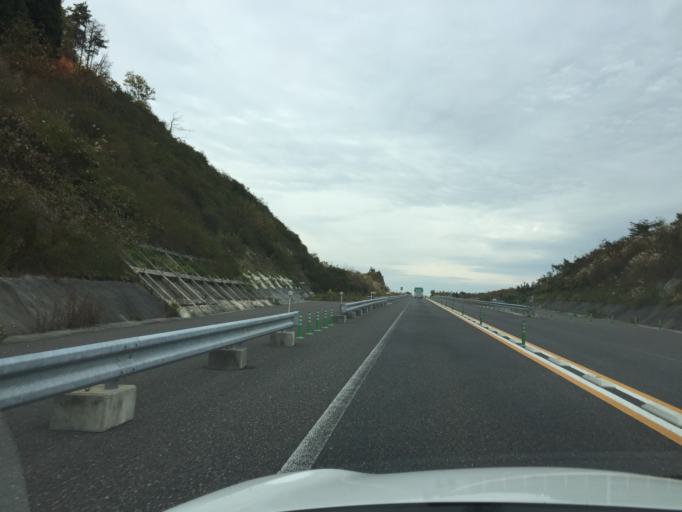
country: JP
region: Fukushima
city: Ishikawa
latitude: 37.2175
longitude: 140.5424
